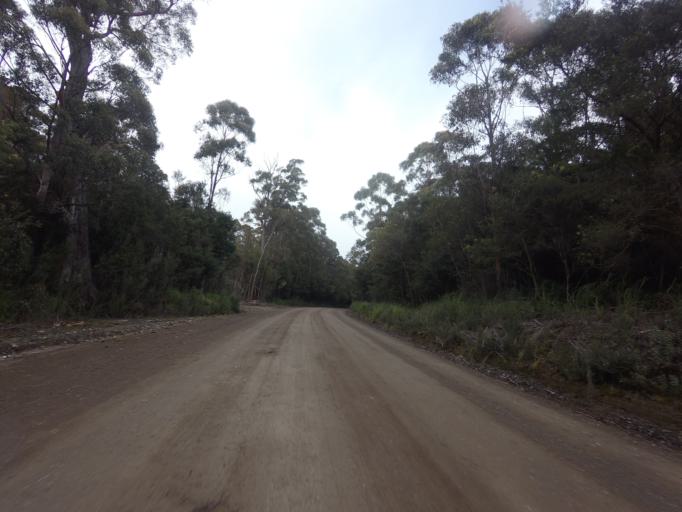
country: AU
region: Tasmania
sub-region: Huon Valley
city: Geeveston
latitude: -43.5156
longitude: 146.8860
